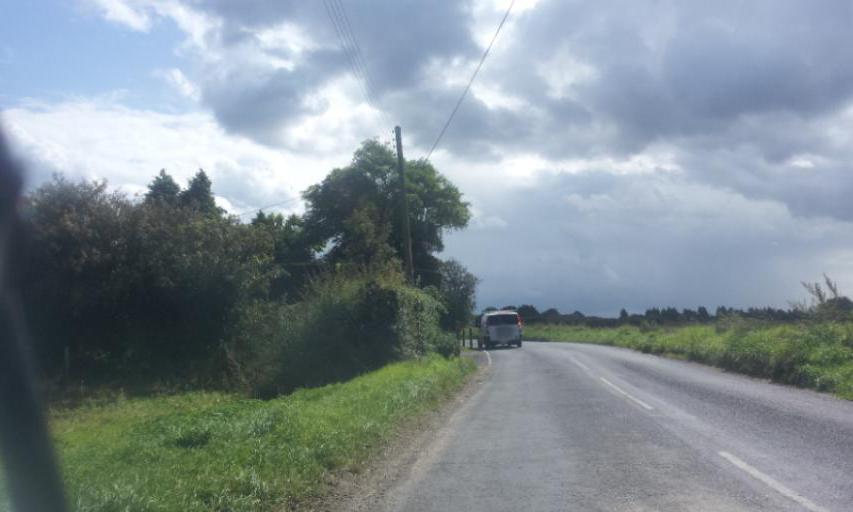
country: GB
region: England
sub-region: Kent
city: Sittingbourne
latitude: 51.3256
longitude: 0.7072
